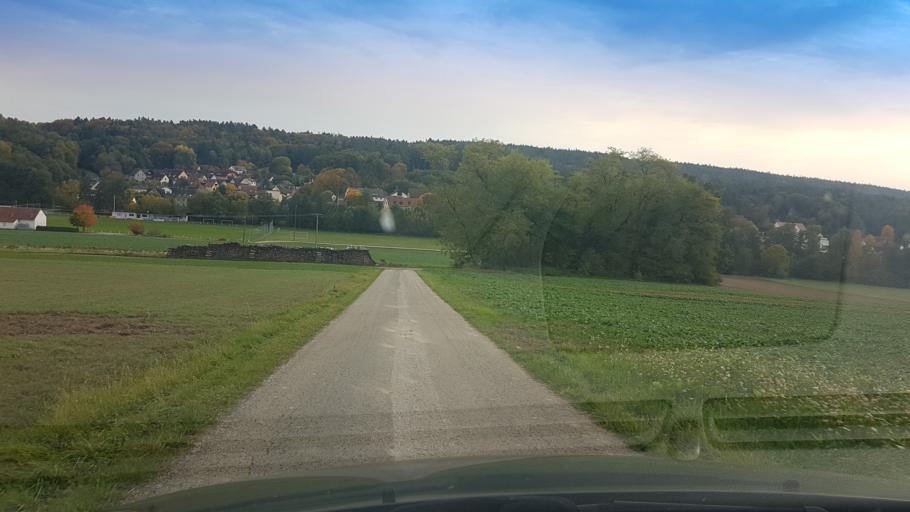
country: DE
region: Bavaria
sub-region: Upper Franconia
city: Gundelsheim
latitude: 49.9713
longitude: 10.9265
